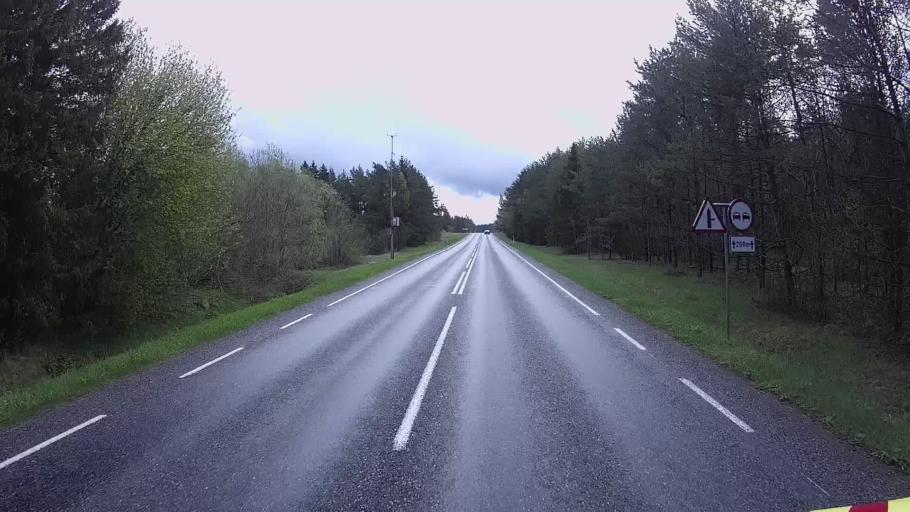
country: EE
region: Hiiumaa
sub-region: Kaerdla linn
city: Kardla
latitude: 58.9725
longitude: 22.8231
